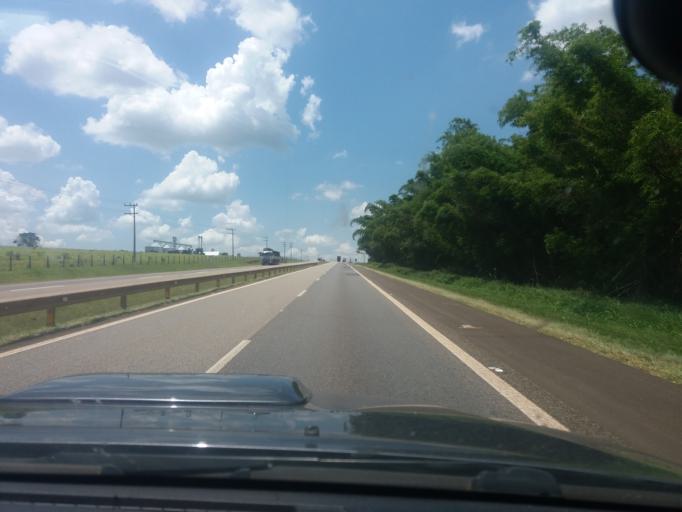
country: BR
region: Sao Paulo
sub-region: Itapetininga
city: Itapetininga
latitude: -23.5279
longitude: -47.9649
